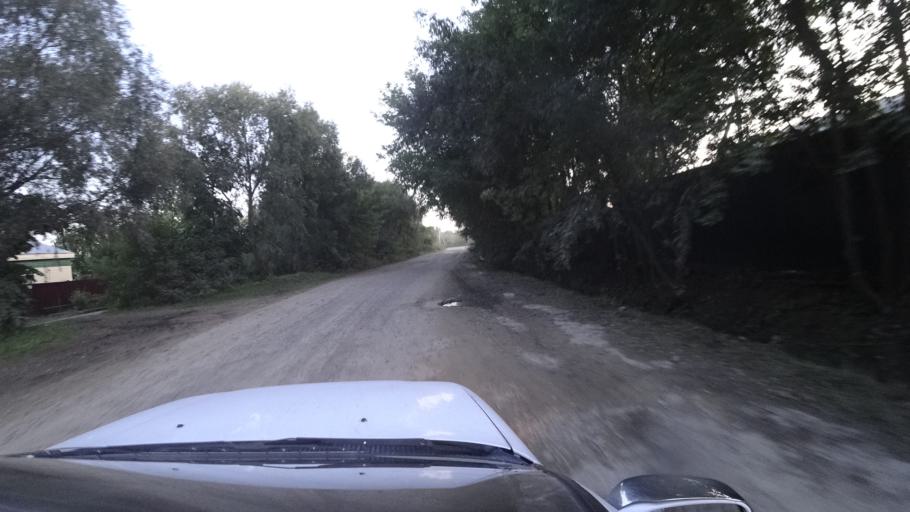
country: RU
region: Primorskiy
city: Dal'nerechensk
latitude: 45.9351
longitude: 133.7588
